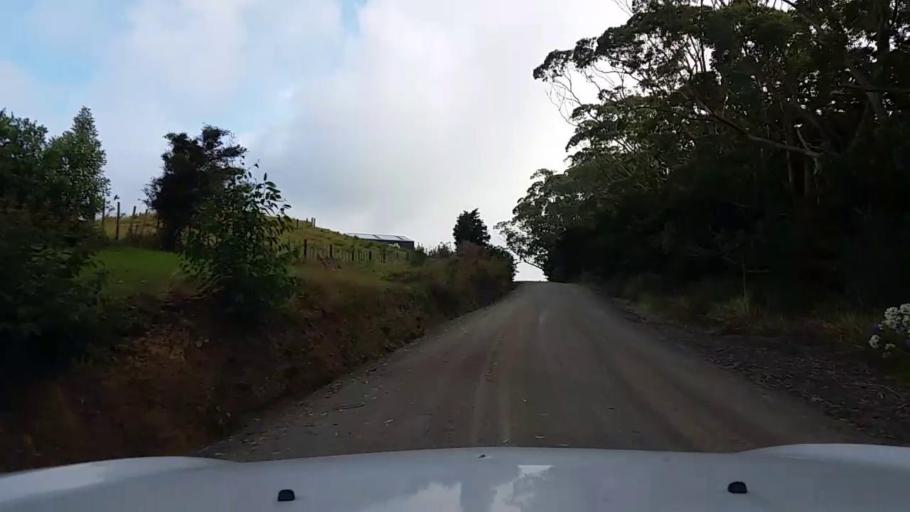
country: NZ
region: Northland
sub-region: Whangarei
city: Maungatapere
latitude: -35.6706
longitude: 174.1749
